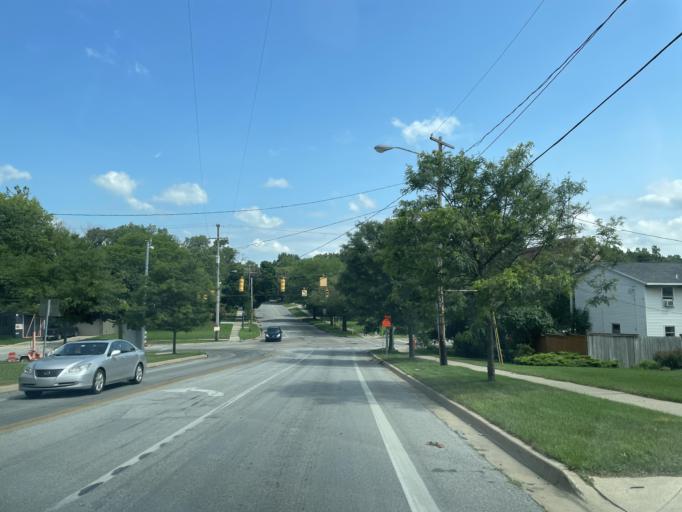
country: US
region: Michigan
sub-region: Kent County
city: East Grand Rapids
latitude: 42.9404
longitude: -85.6248
